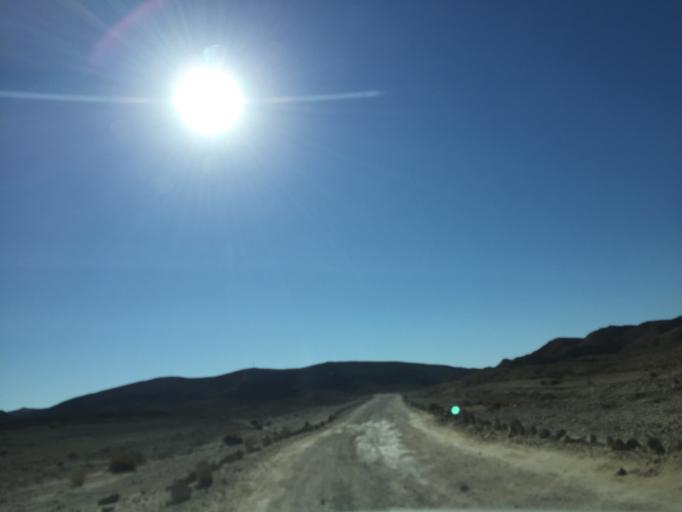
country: IL
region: Southern District
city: Mitzpe Ramon
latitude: 30.6010
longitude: 34.8952
